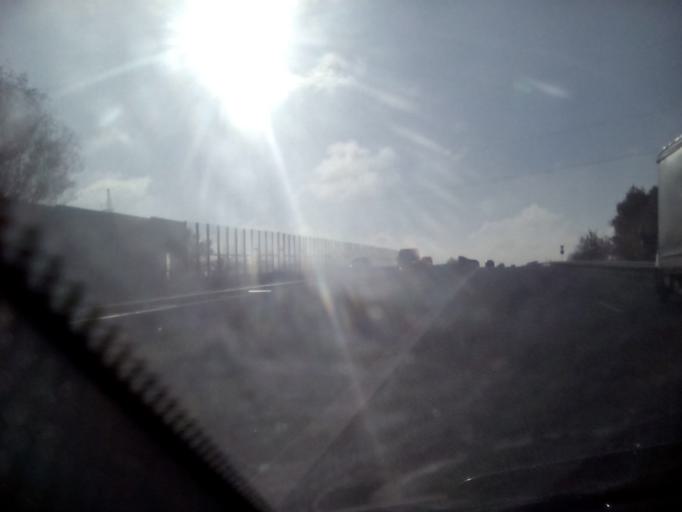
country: PL
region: Masovian Voivodeship
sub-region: Powiat grojecki
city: Grojec
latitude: 51.8509
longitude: 20.8687
